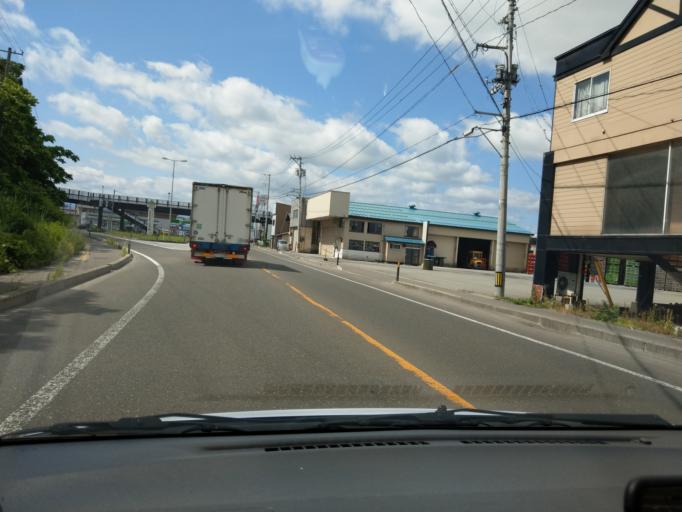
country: JP
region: Akita
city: Yuzawa
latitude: 39.1771
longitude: 140.4928
